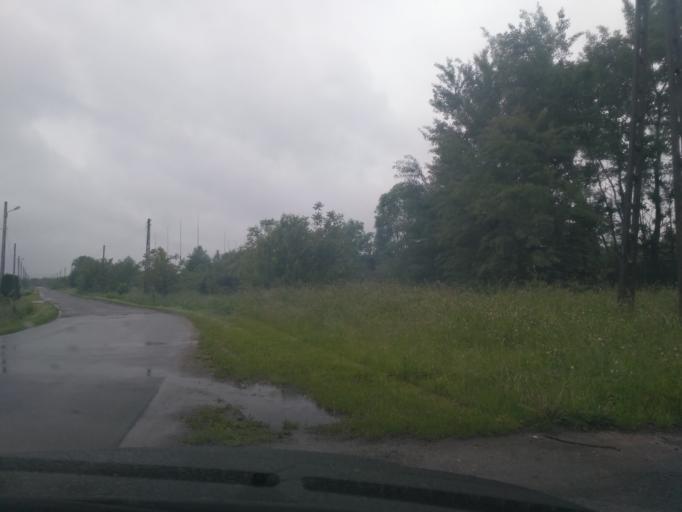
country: PL
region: Subcarpathian Voivodeship
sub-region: Powiat jasielski
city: Jaslo
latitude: 49.7443
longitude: 21.5069
